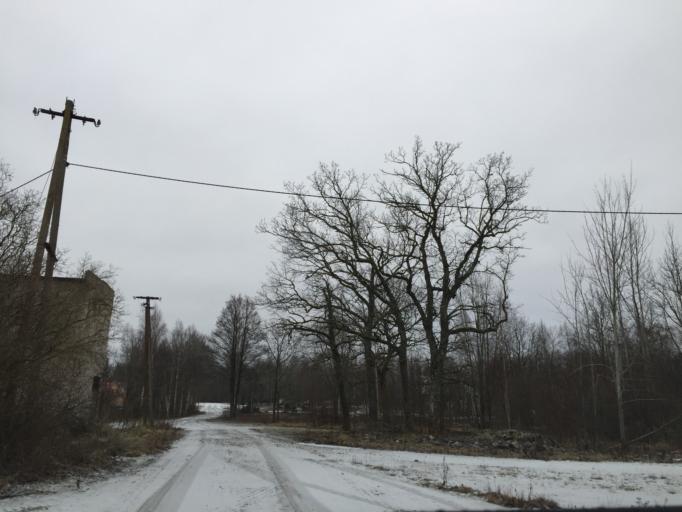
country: EE
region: Saare
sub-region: Orissaare vald
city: Orissaare
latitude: 58.6822
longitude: 23.1939
